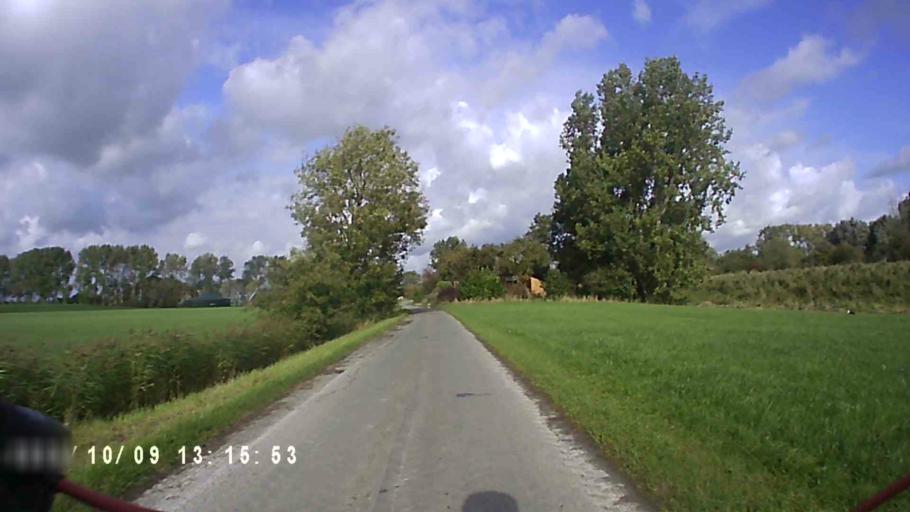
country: NL
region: Groningen
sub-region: Gemeente Zuidhorn
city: Aduard
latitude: 53.2568
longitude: 6.4331
